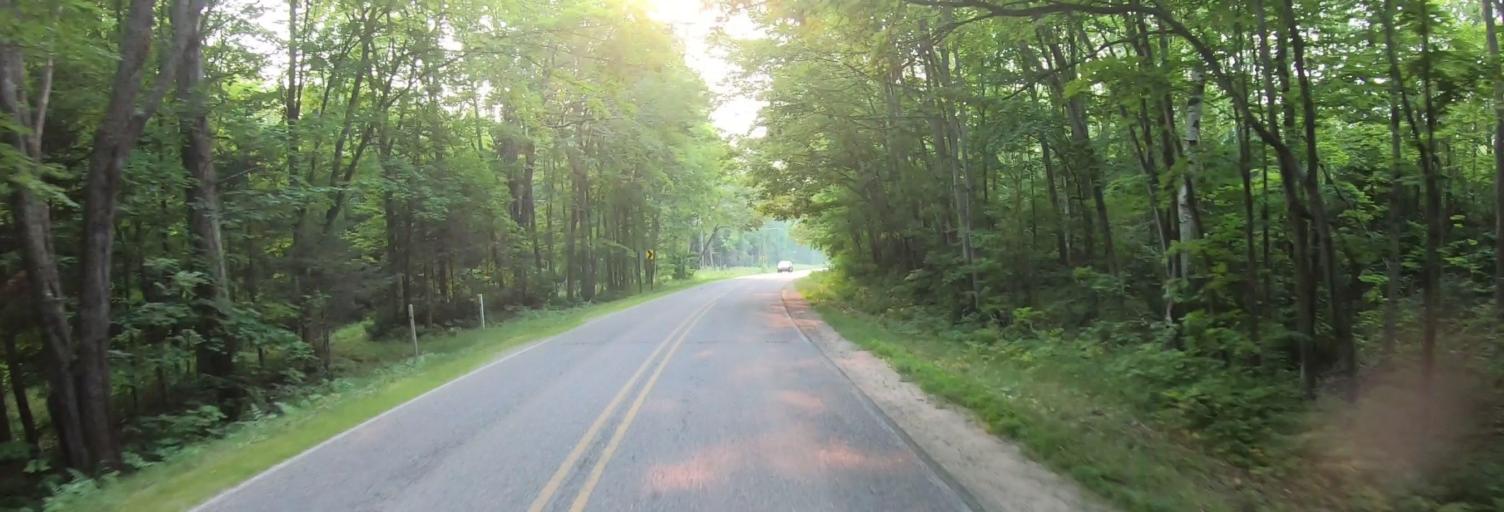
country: US
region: Michigan
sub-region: Chippewa County
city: Sault Ste. Marie
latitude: 46.4813
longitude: -84.6572
